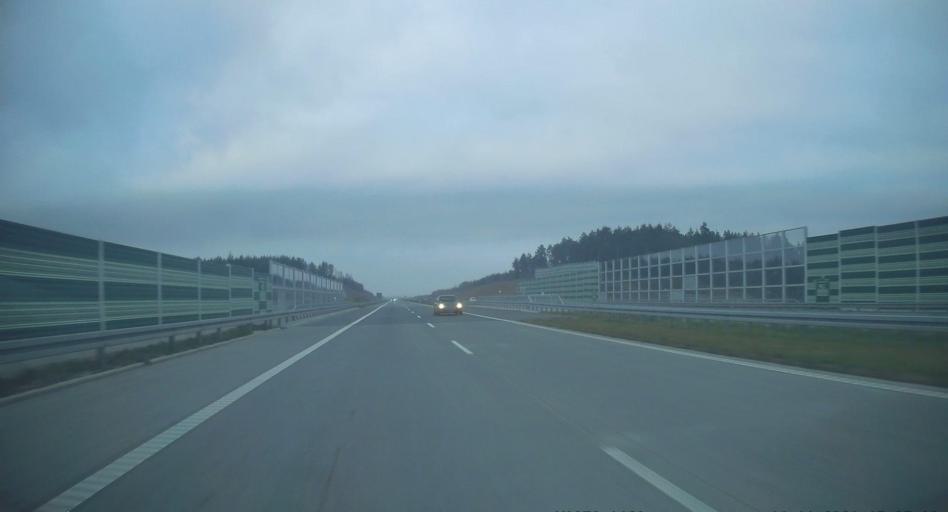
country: PL
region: Silesian Voivodeship
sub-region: Powiat czestochowski
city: Starcza
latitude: 50.7088
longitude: 19.0566
